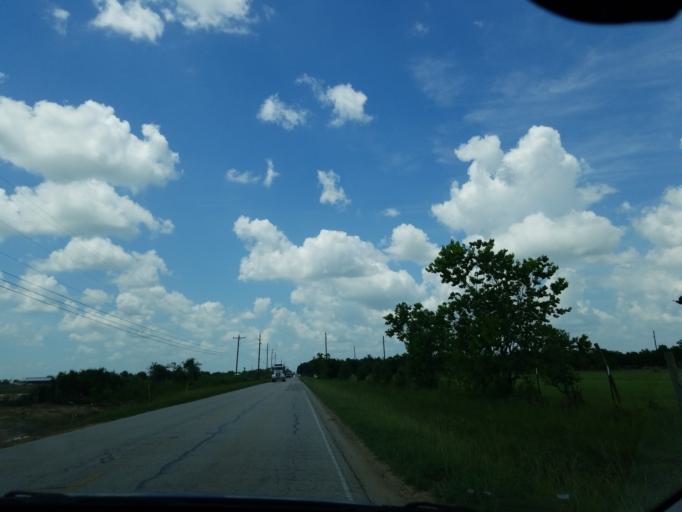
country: US
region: Texas
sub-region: Harris County
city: Katy
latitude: 29.8534
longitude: -95.8069
